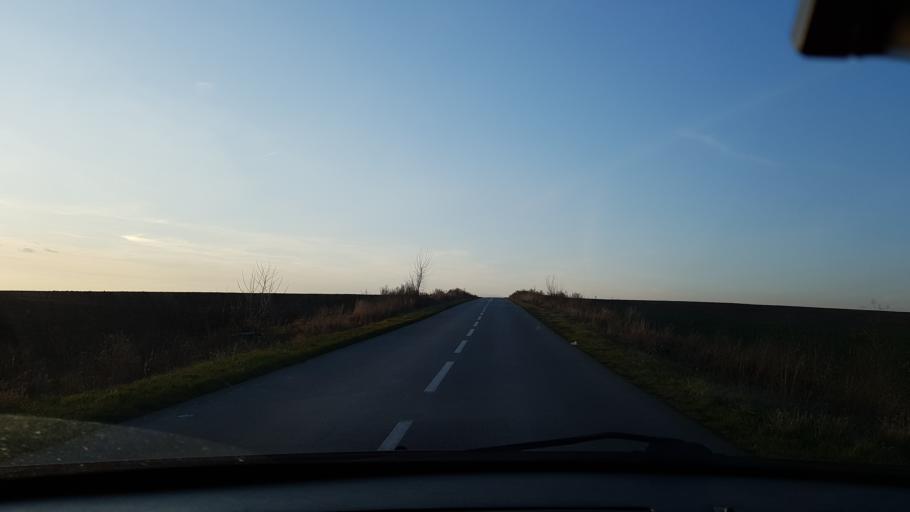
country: PL
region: Lower Silesian Voivodeship
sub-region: Powiat zabkowicki
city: Henrykow
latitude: 50.6695
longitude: 16.9719
